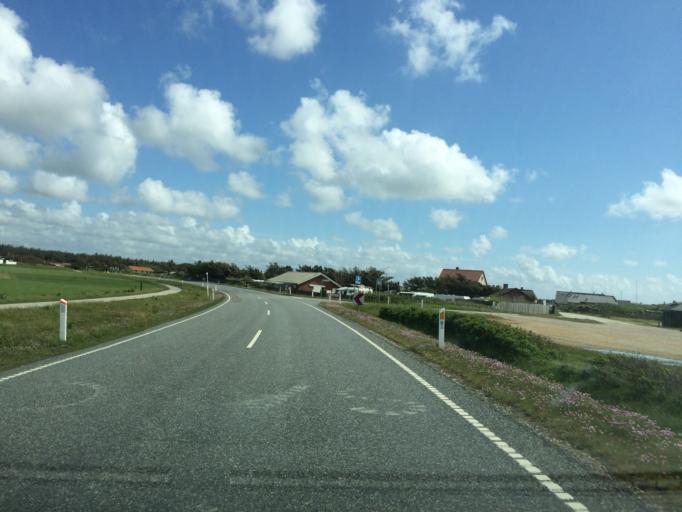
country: DK
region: Central Jutland
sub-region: Holstebro Kommune
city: Ulfborg
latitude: 56.3237
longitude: 8.1240
